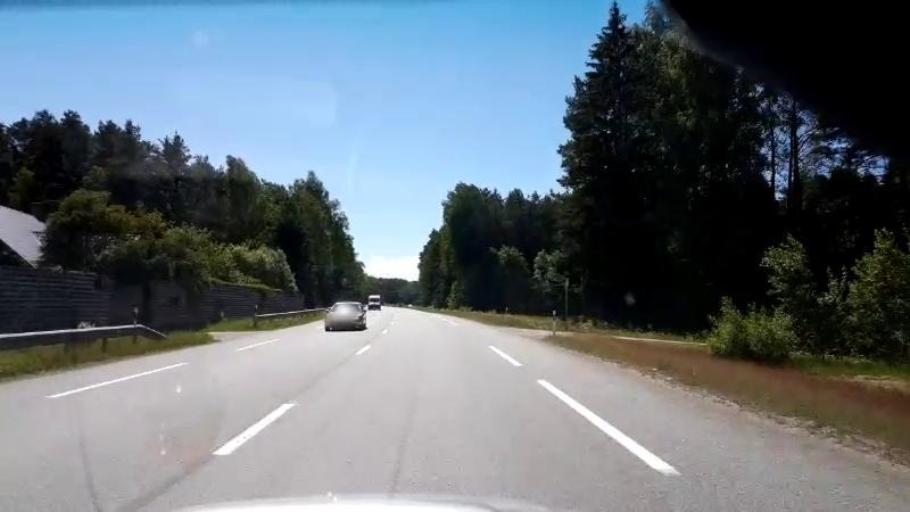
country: LV
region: Saulkrastu
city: Saulkrasti
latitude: 57.4370
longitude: 24.4299
